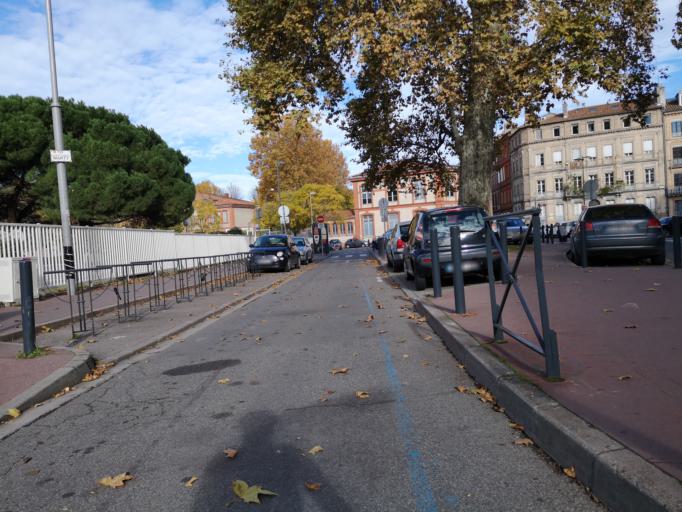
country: FR
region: Midi-Pyrenees
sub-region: Departement de la Haute-Garonne
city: Toulouse
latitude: 43.6058
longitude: 1.4381
